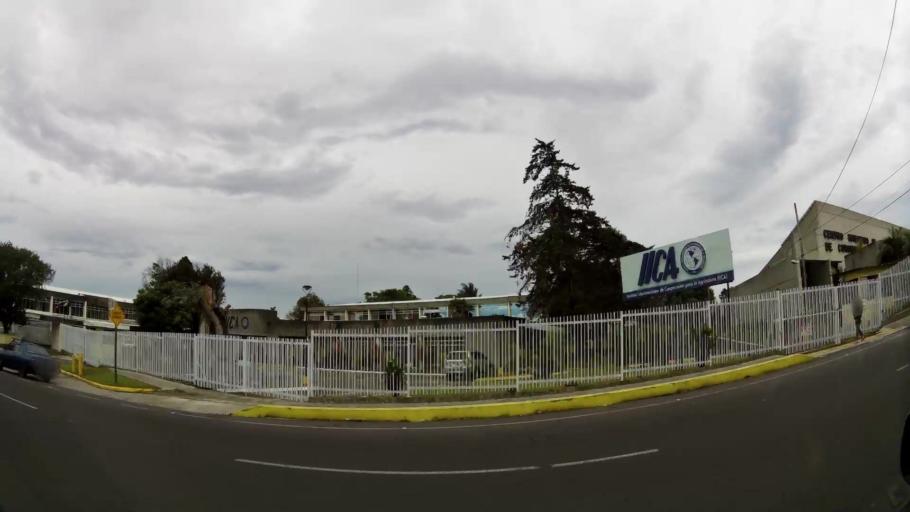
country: CR
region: San Jose
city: Ipis
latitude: 9.9693
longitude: -84.0168
